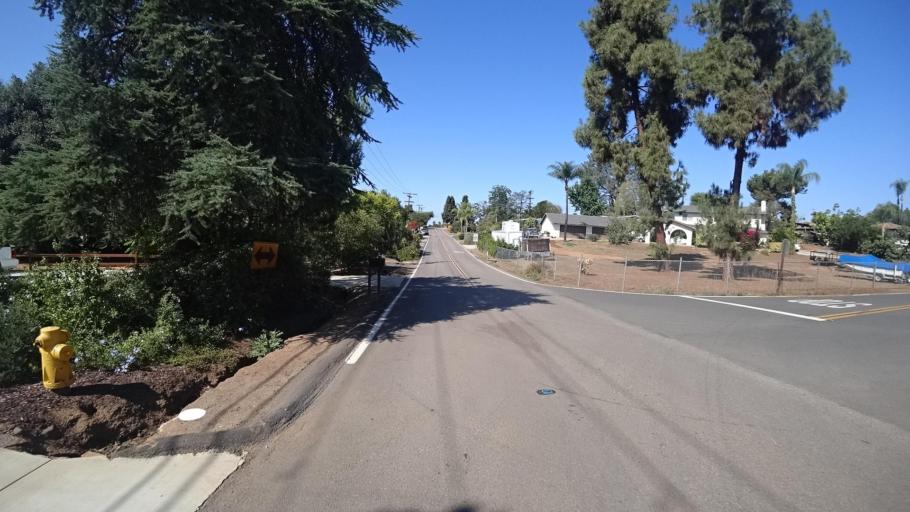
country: US
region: California
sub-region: San Diego County
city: Granite Hills
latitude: 32.7913
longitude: -116.9008
